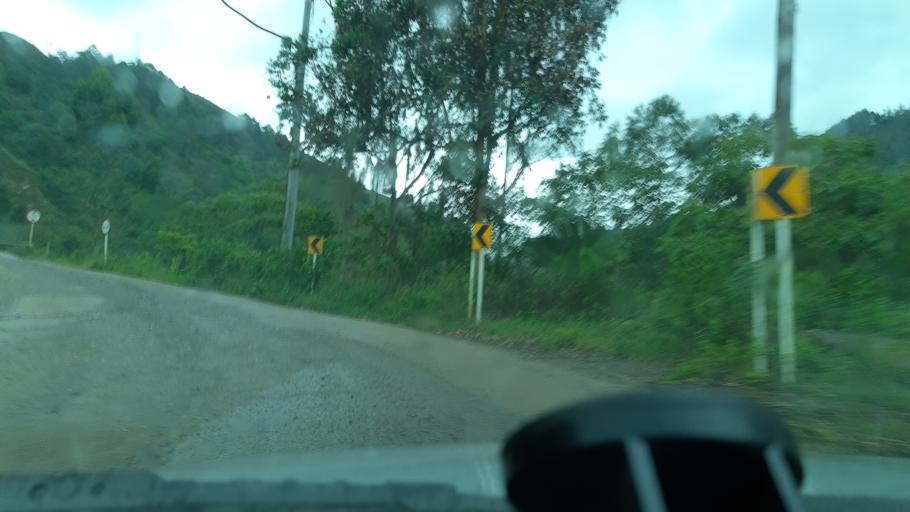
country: CO
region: Boyaca
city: Chinavita
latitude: 5.2148
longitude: -73.3909
